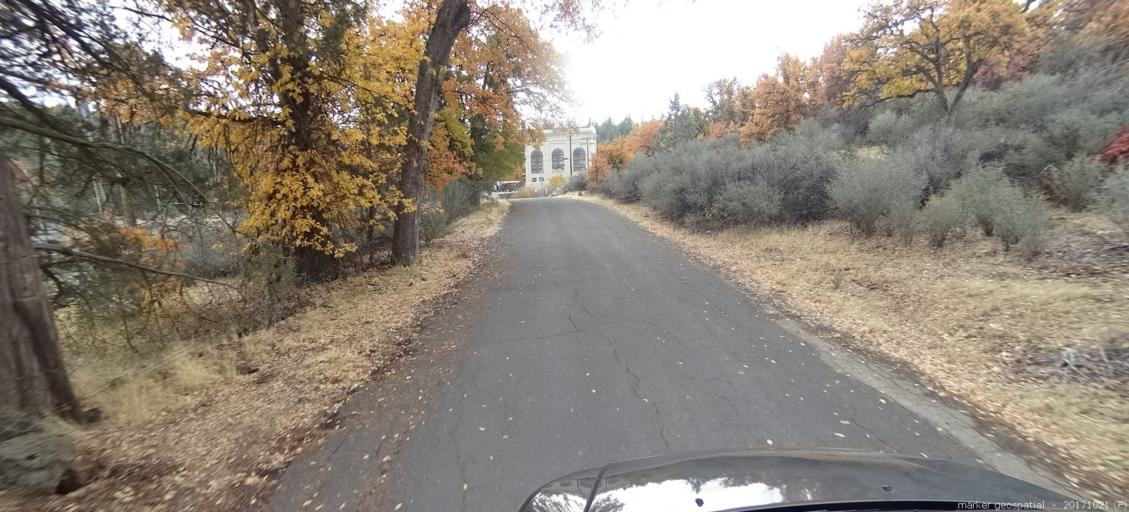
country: US
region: California
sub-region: Shasta County
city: Burney
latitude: 40.9307
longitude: -121.5450
